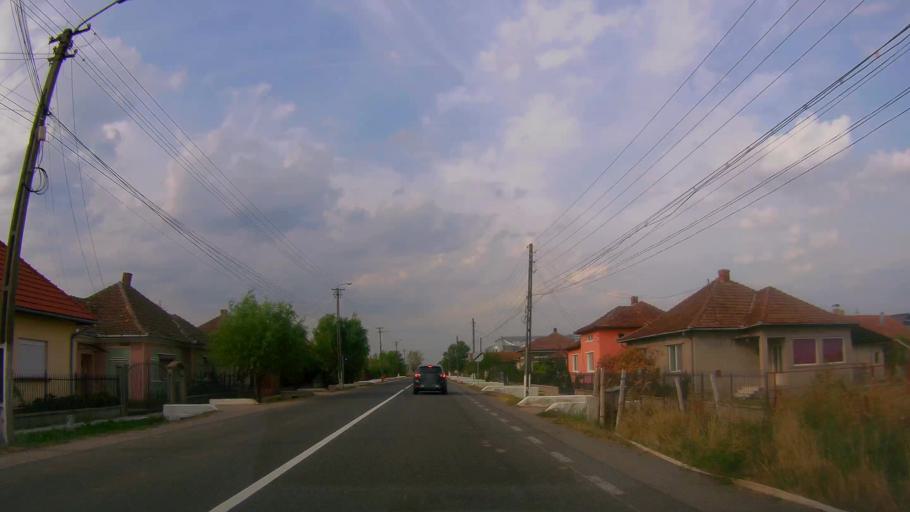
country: RO
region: Satu Mare
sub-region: Oras Ardud
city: Ardud
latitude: 47.6284
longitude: 22.8775
